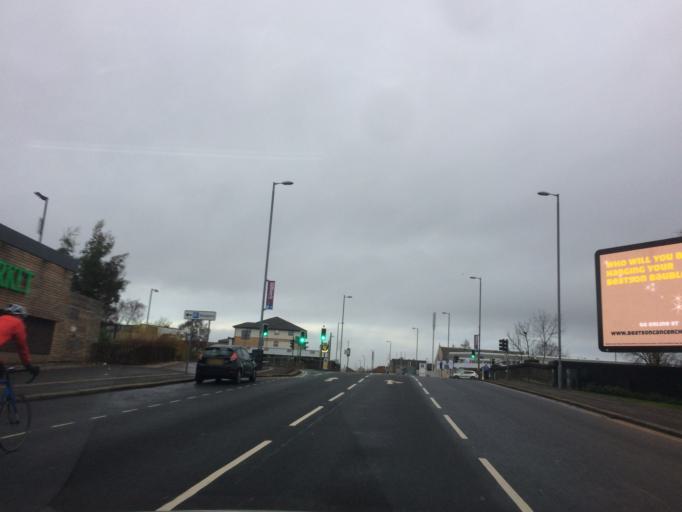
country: GB
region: Scotland
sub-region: East Renfrewshire
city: Giffnock
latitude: 55.8056
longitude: -4.2944
